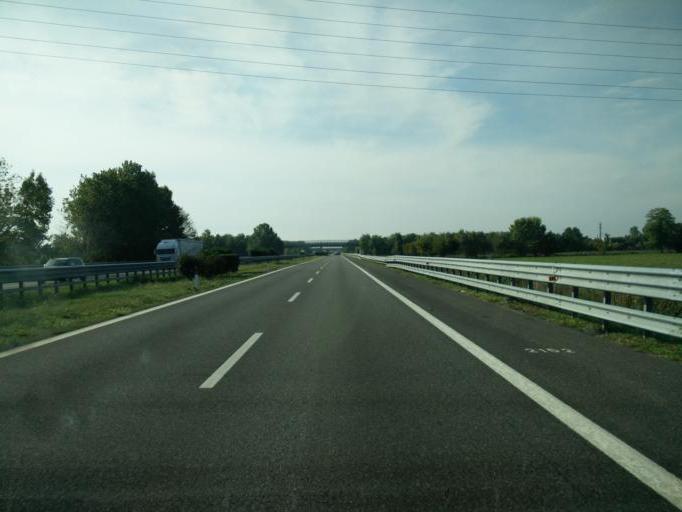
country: IT
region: Lombardy
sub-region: Provincia di Brescia
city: San Gervasio Bresciano
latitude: 45.3174
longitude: 10.1456
